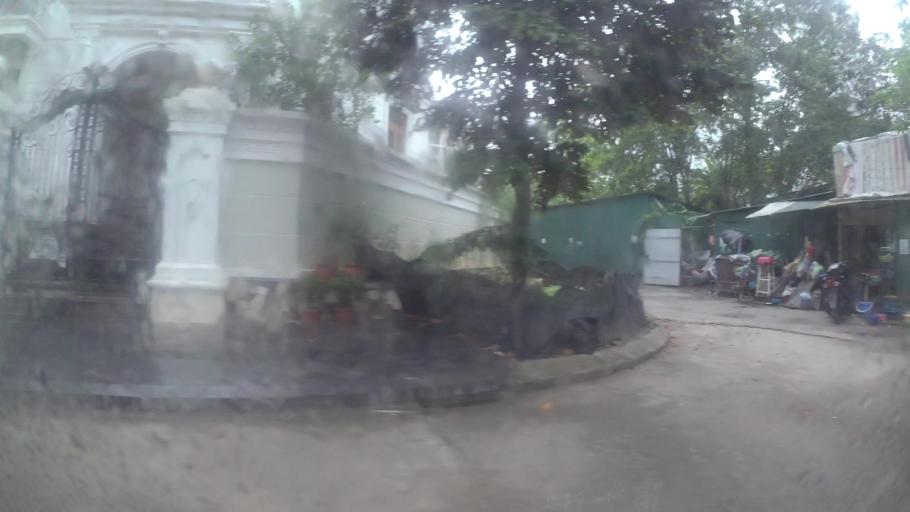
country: VN
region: Ha Noi
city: Cau Giay
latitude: 21.0202
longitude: 105.7902
